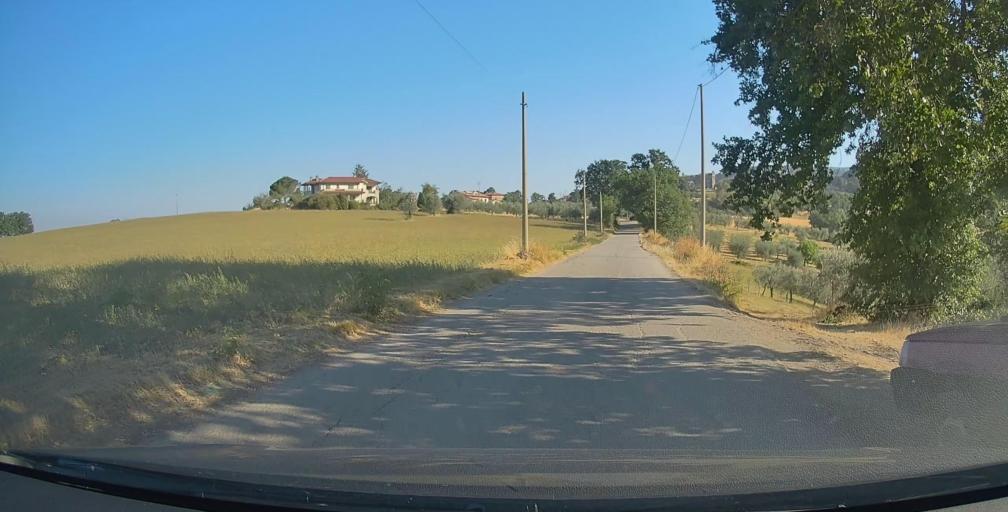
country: IT
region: Umbria
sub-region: Provincia di Terni
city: Calvi dell'Umbria
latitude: 42.3882
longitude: 12.5675
